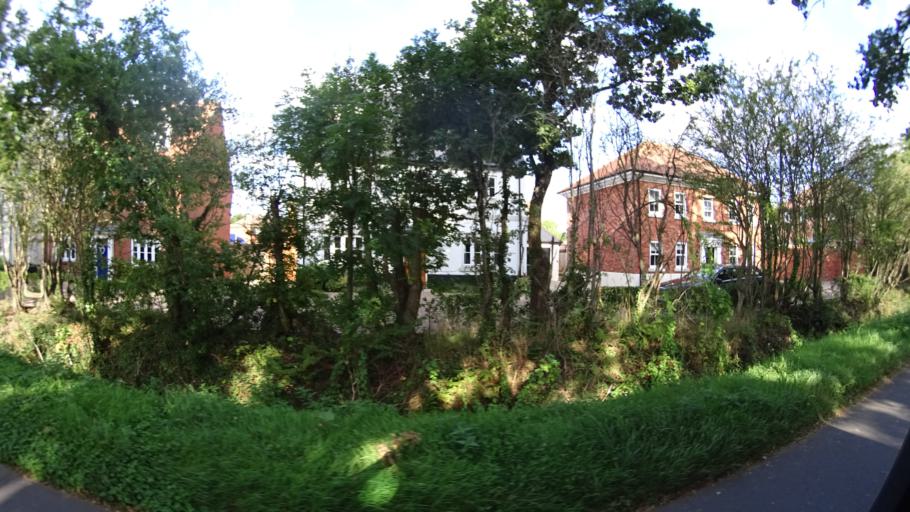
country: GB
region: England
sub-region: Dorset
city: Lytchett Matravers
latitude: 50.7396
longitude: -2.0453
